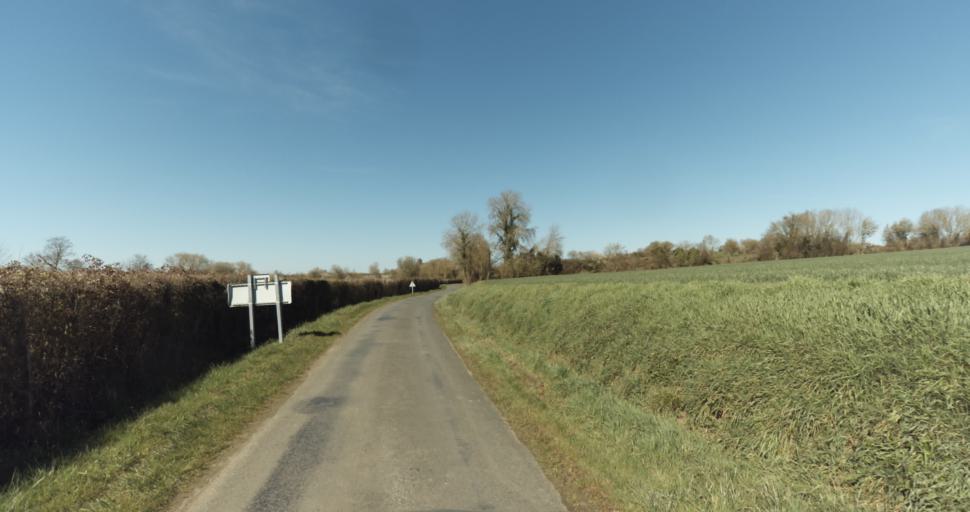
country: FR
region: Lower Normandy
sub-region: Departement du Calvados
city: Saint-Pierre-sur-Dives
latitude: 49.0545
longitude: -0.0239
